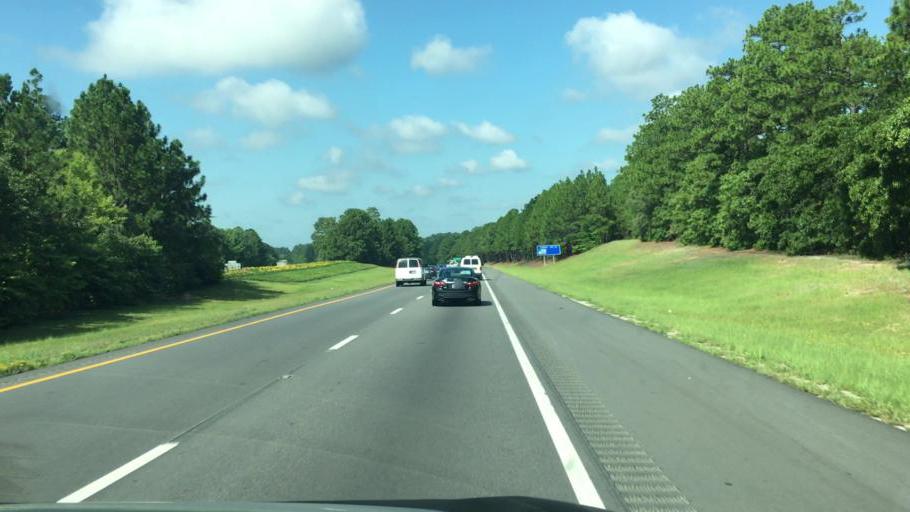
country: US
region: North Carolina
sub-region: Cumberland County
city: Hope Mills
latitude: 34.9705
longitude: -78.8741
